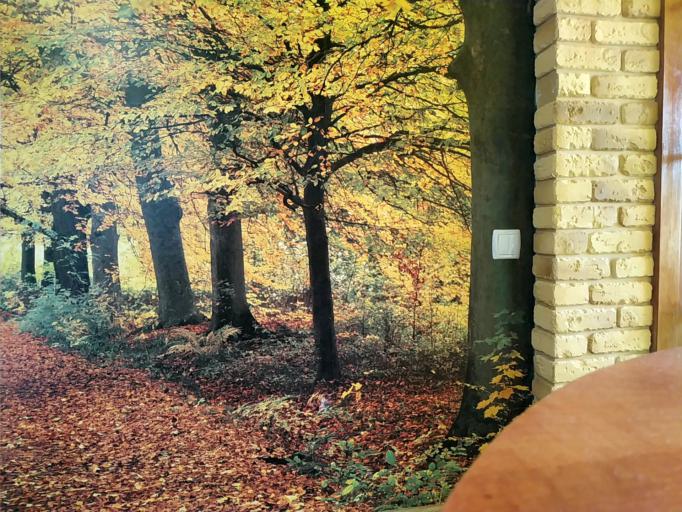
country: RU
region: Pskov
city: Dno
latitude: 57.9109
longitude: 30.1787
